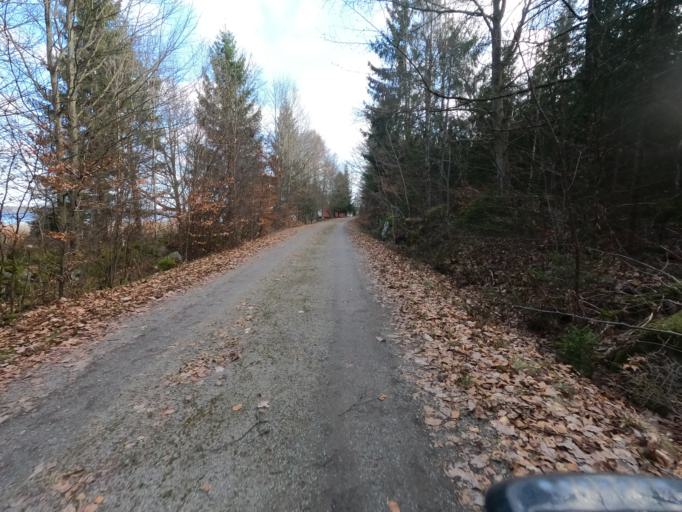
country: SE
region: Kronoberg
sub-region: Vaxjo Kommun
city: Gemla
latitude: 56.6689
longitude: 14.6204
